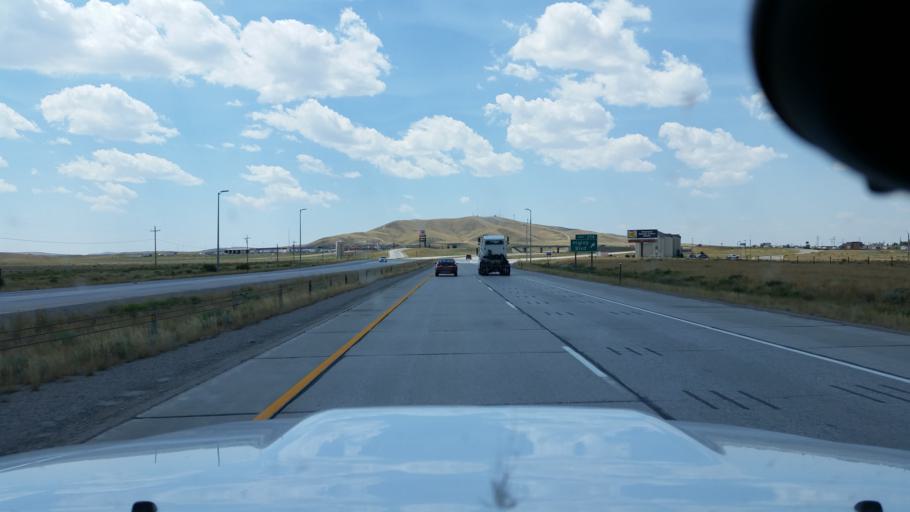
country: US
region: Wyoming
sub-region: Carbon County
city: Rawlins
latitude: 41.7816
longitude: -107.2159
